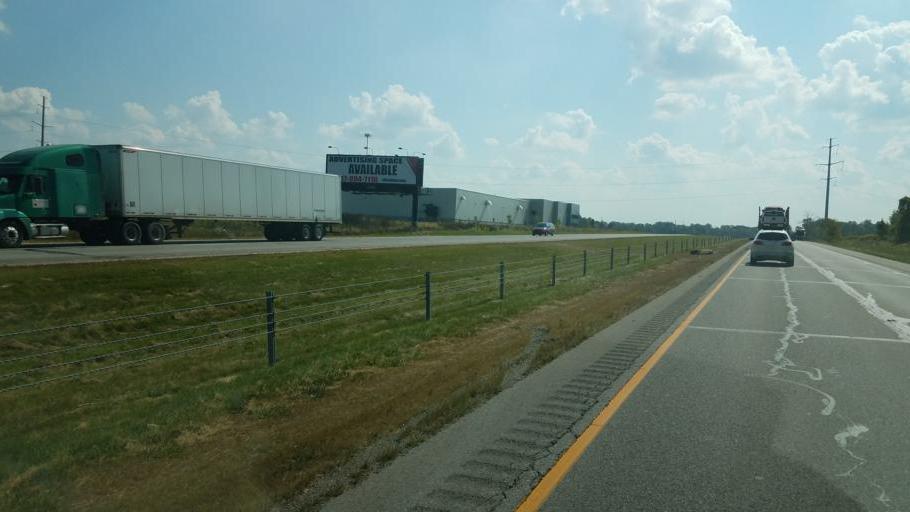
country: US
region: Indiana
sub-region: Allen County
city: Leo-Cedarville
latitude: 41.2695
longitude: -85.0870
